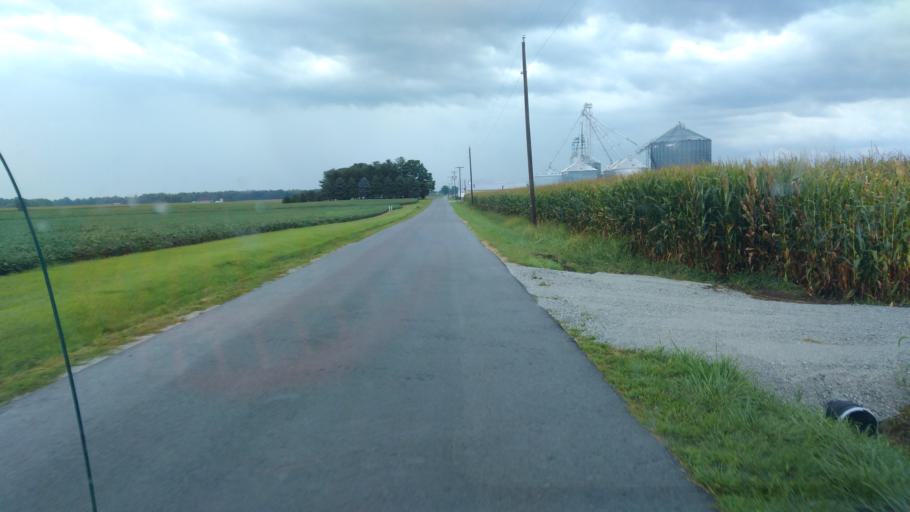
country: US
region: Ohio
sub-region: Hardin County
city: Kenton
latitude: 40.6894
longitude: -83.6314
